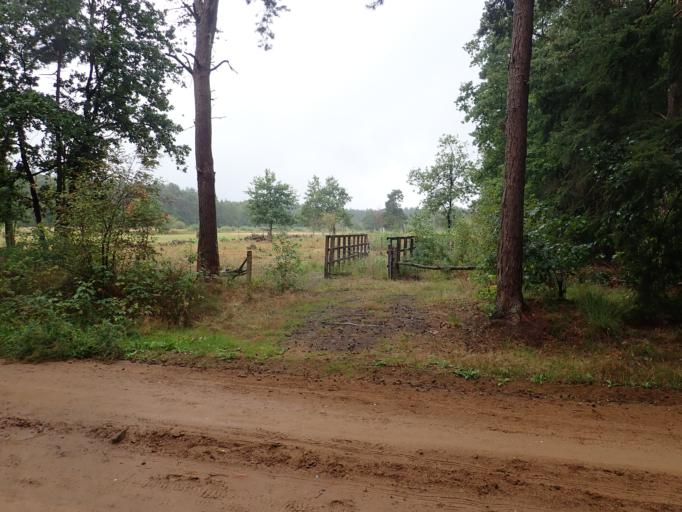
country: BE
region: Flanders
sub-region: Provincie Antwerpen
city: Lille
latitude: 51.2790
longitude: 4.8199
